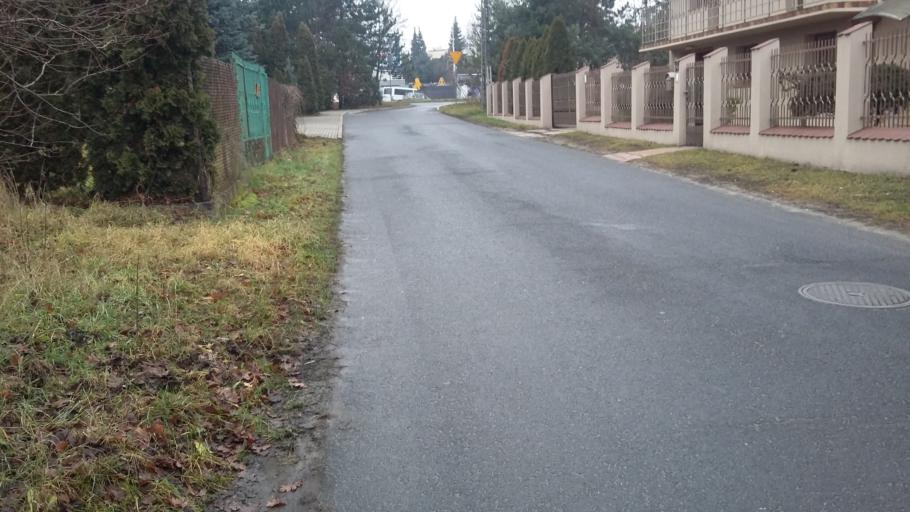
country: PL
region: Lodz Voivodeship
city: Lodz
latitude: 51.7386
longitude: 19.4141
